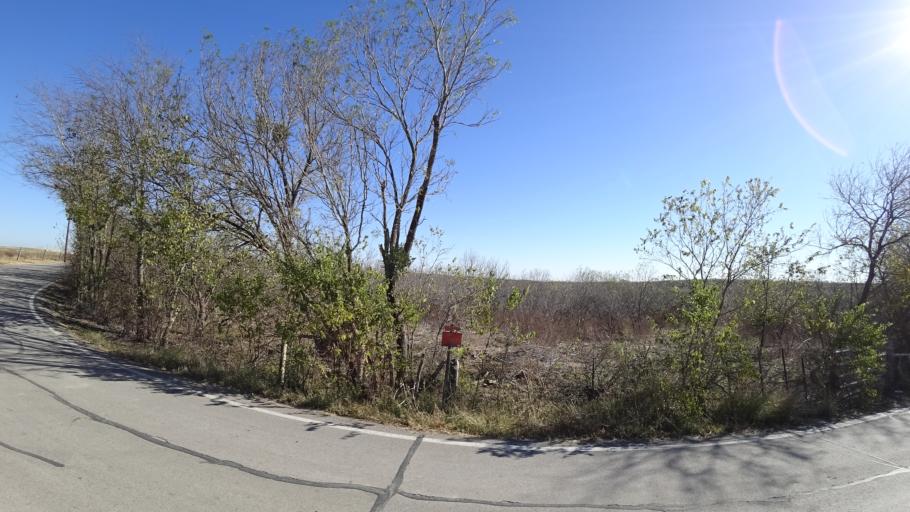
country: US
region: Texas
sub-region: Travis County
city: Onion Creek
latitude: 30.1138
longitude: -97.6727
